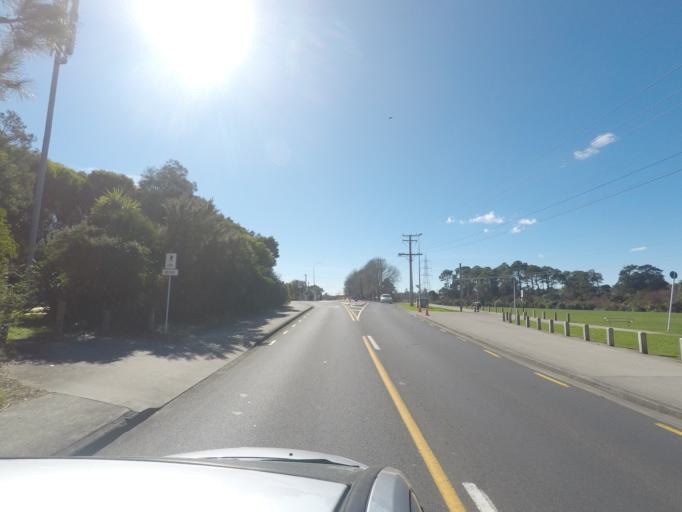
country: NZ
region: Auckland
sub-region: Auckland
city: Waitakere
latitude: -36.9234
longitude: 174.6906
